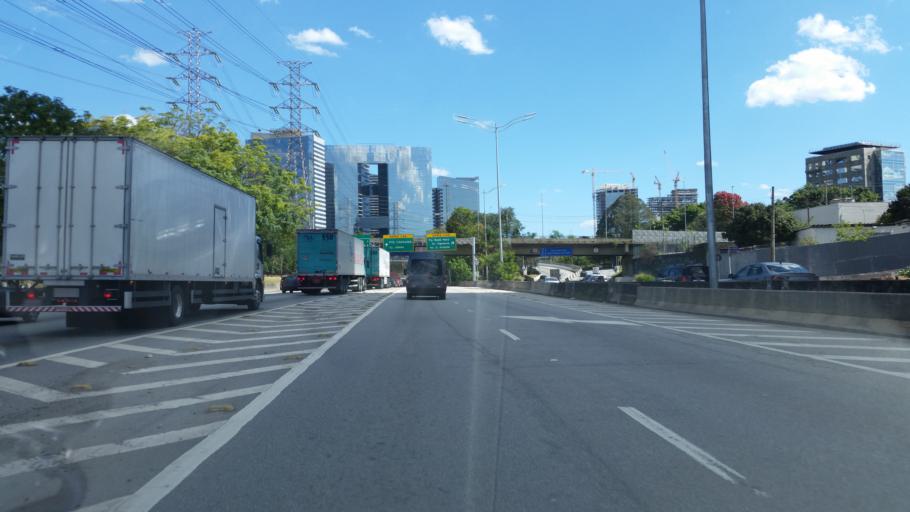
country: BR
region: Sao Paulo
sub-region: Taboao Da Serra
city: Taboao da Serra
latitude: -23.6166
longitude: -46.7015
